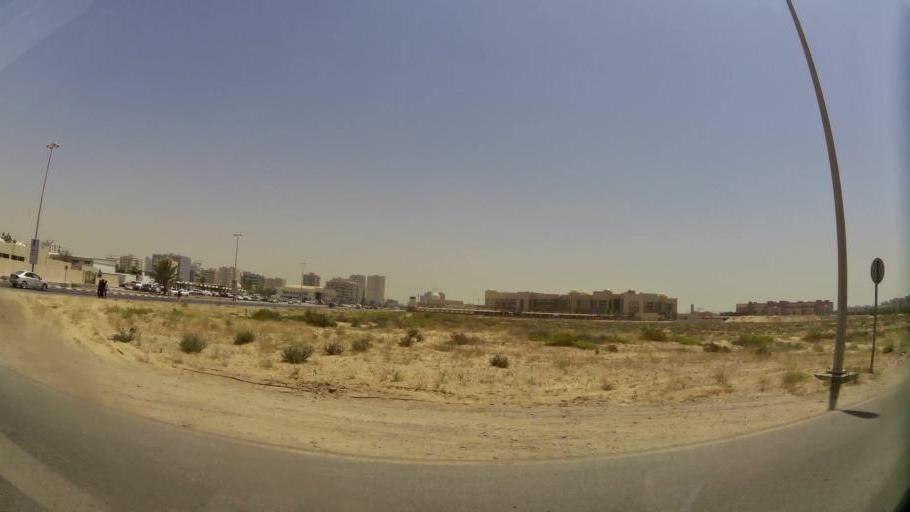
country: AE
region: Ajman
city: Ajman
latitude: 25.4146
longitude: 55.5111
